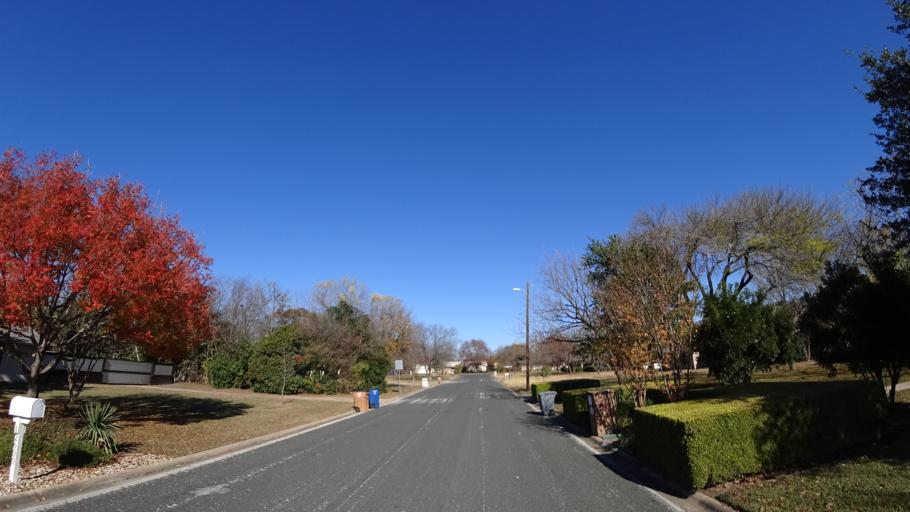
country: US
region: Texas
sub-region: Travis County
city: Wells Branch
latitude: 30.4199
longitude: -97.6978
